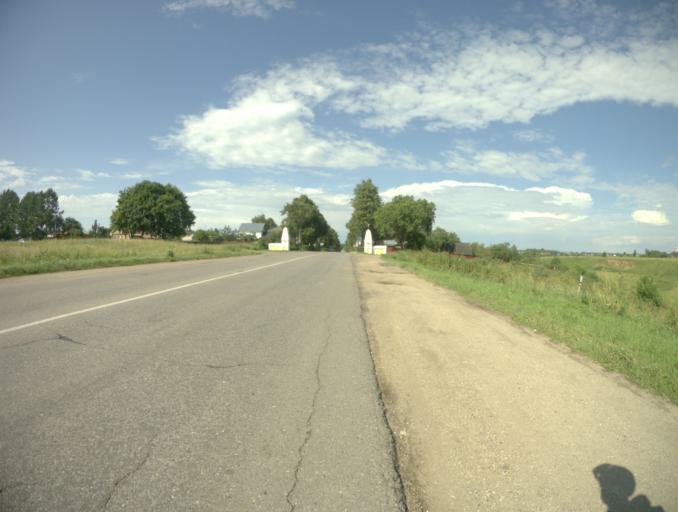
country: RU
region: Vladimir
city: Suzdal'
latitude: 56.4063
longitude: 40.4457
